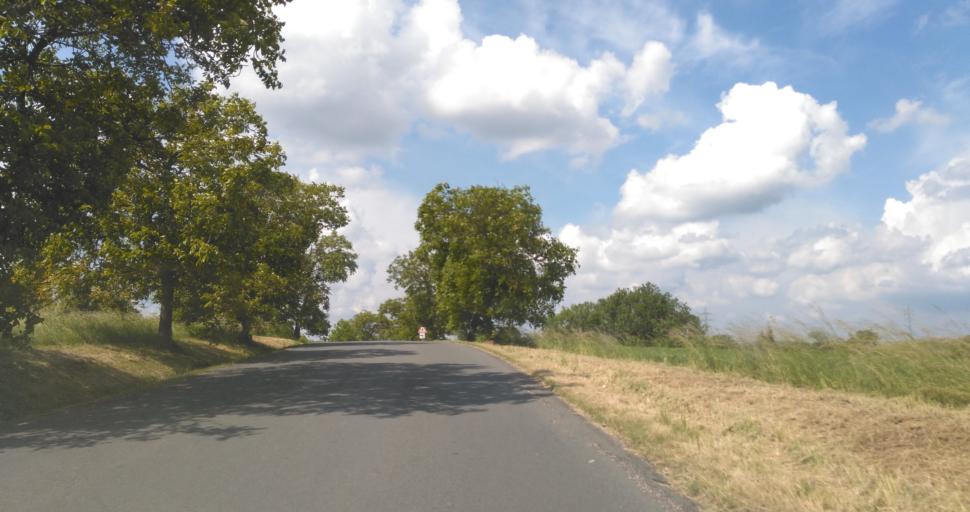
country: CZ
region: Central Bohemia
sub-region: Okres Beroun
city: Beroun
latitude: 49.9355
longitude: 14.0727
